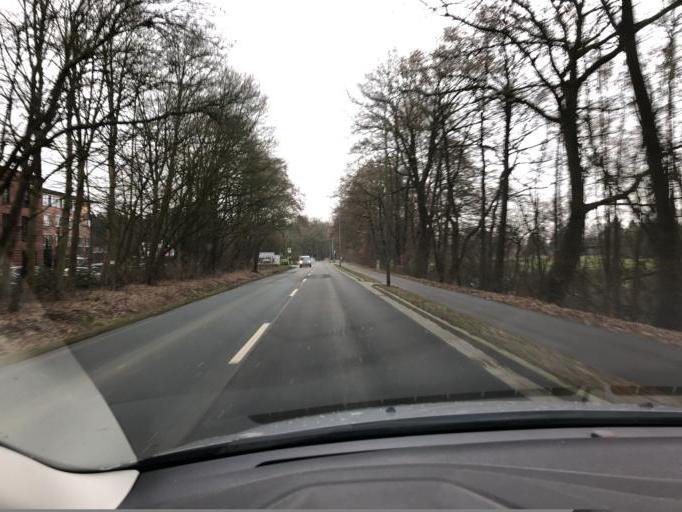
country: DE
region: Lower Saxony
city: Oldenburg
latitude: 53.1639
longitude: 8.1623
